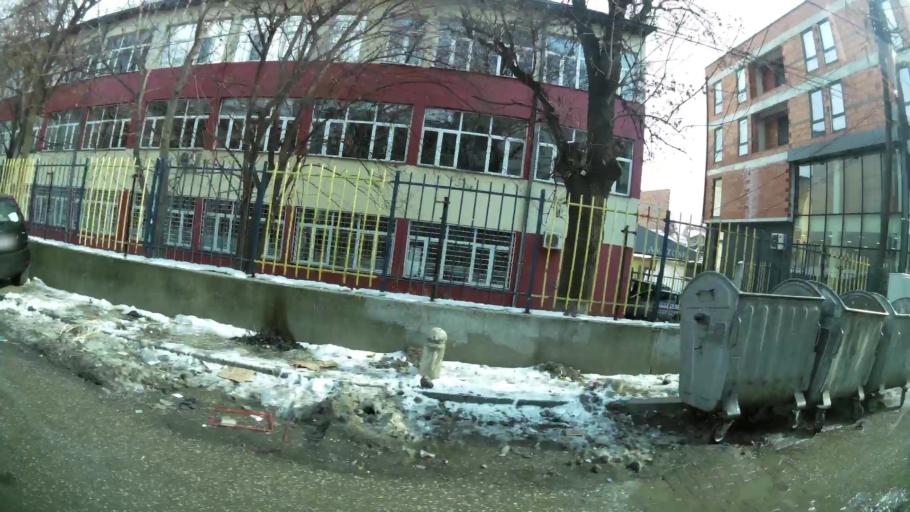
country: MK
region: Karpos
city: Skopje
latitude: 42.0049
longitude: 21.4360
